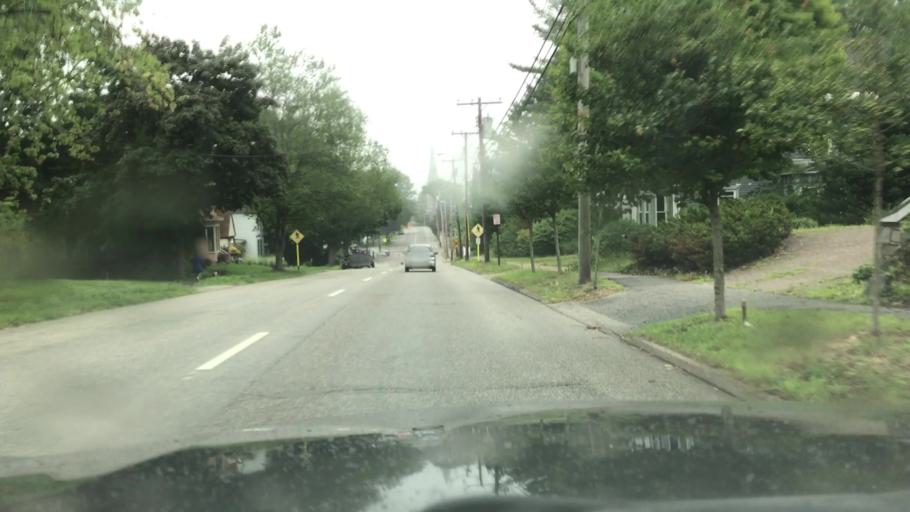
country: US
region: Maine
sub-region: Cumberland County
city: Brunswick
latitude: 43.9131
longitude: -69.9743
